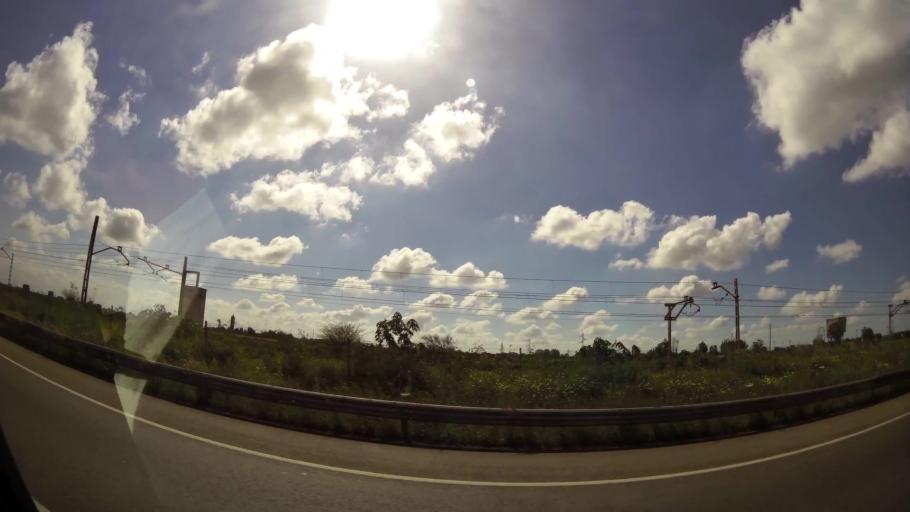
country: MA
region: Chaouia-Ouardigha
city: Nouaseur
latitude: 33.4183
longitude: -7.6270
